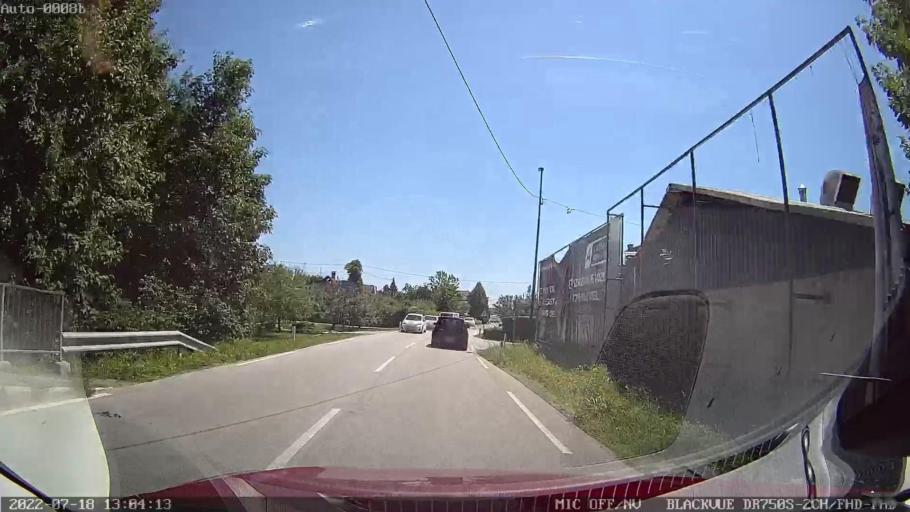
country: SI
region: Brezovica
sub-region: Opstina Ljubljana-Vic-Rudnik
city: Brezovica pri Ljubljani
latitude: 46.0461
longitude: 14.4415
